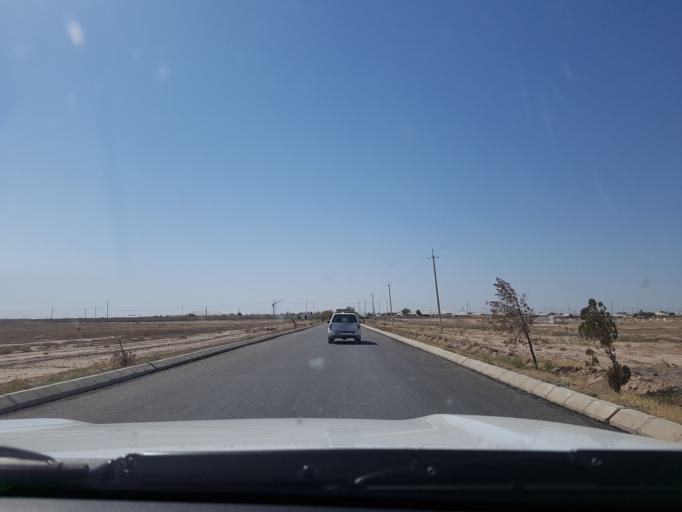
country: IR
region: Razavi Khorasan
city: Sarakhs
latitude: 36.5138
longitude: 61.2296
